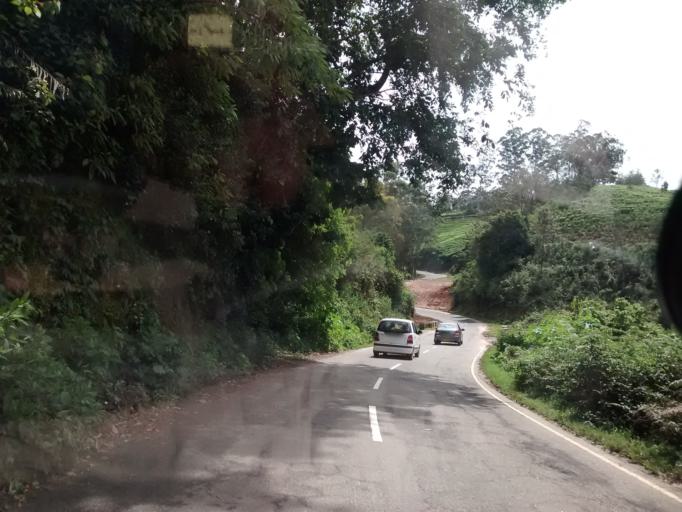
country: IN
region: Kerala
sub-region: Idukki
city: Munnar
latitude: 10.0892
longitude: 77.0849
